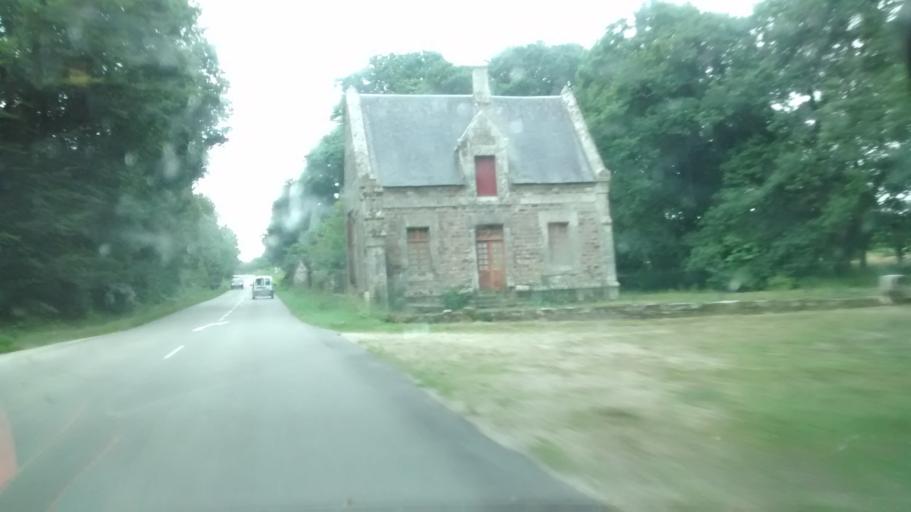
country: FR
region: Brittany
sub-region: Departement du Morbihan
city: Molac
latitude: 47.7571
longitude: -2.4376
